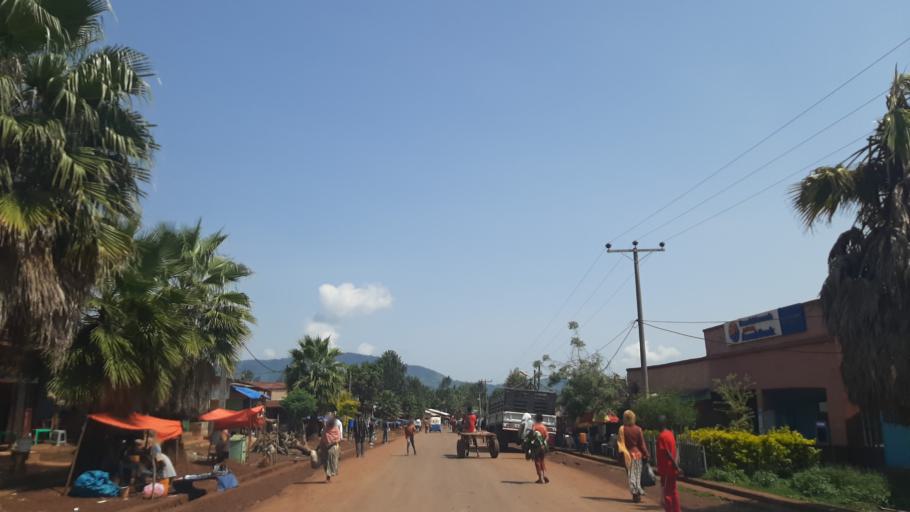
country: ET
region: Oromiya
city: Agaro
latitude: 8.0904
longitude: 36.9506
